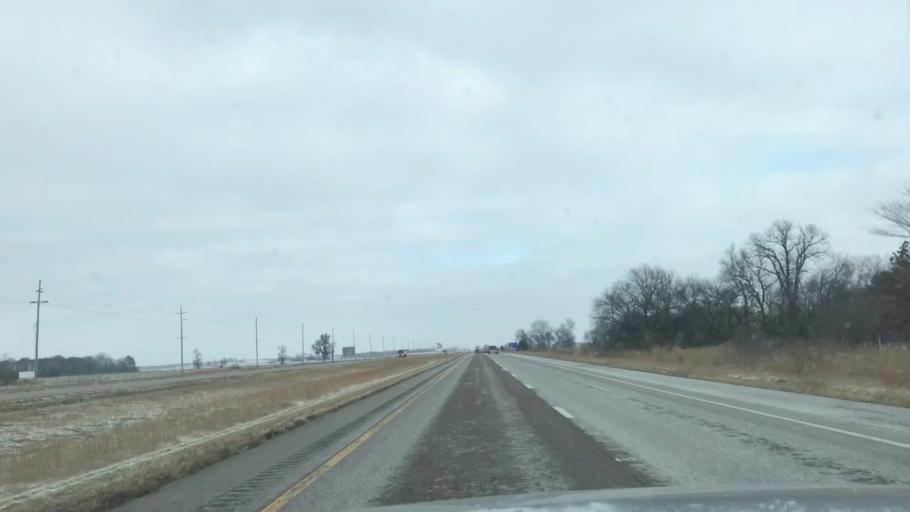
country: US
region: Illinois
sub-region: Macoupin County
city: Staunton
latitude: 38.9892
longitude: -89.7495
